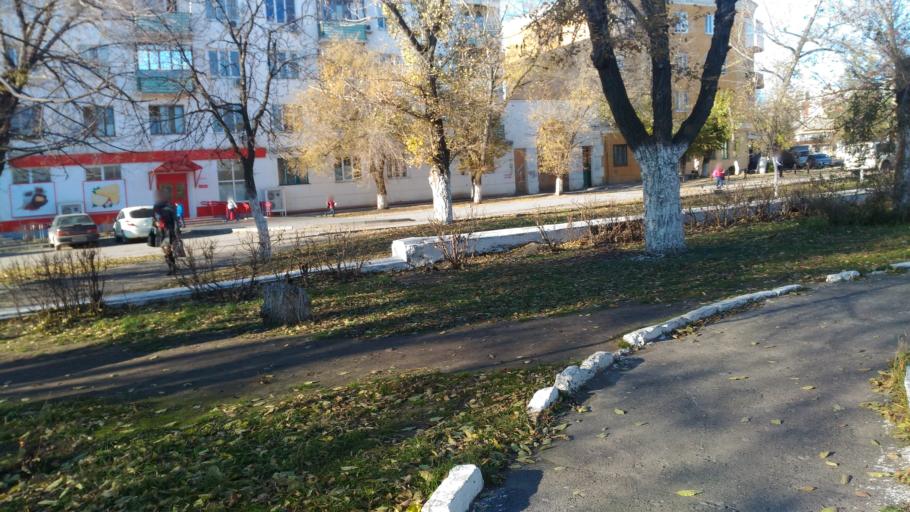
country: RU
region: Volgograd
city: Volgograd
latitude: 48.6593
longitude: 44.4454
